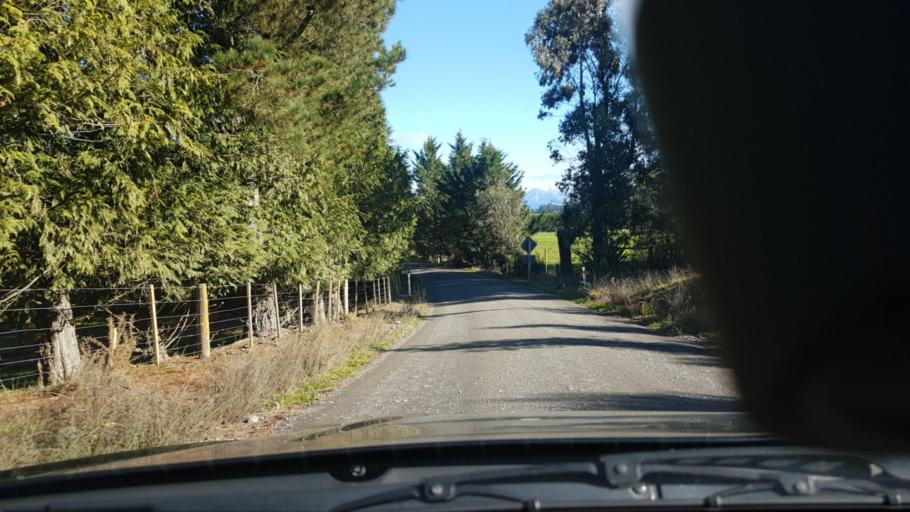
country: NZ
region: Canterbury
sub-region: Waimakariri District
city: Oxford
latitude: -43.2927
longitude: 172.1773
